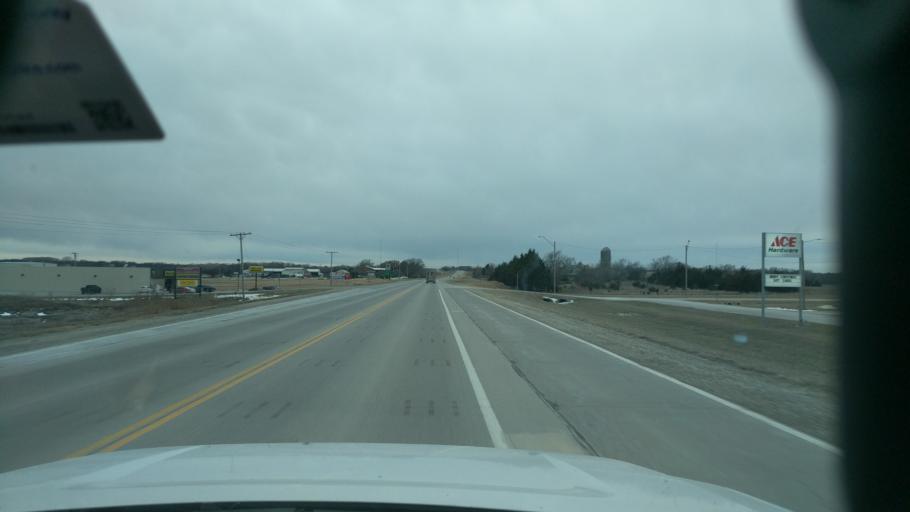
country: US
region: Kansas
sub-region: Marion County
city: Marion
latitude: 38.3627
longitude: -97.0072
